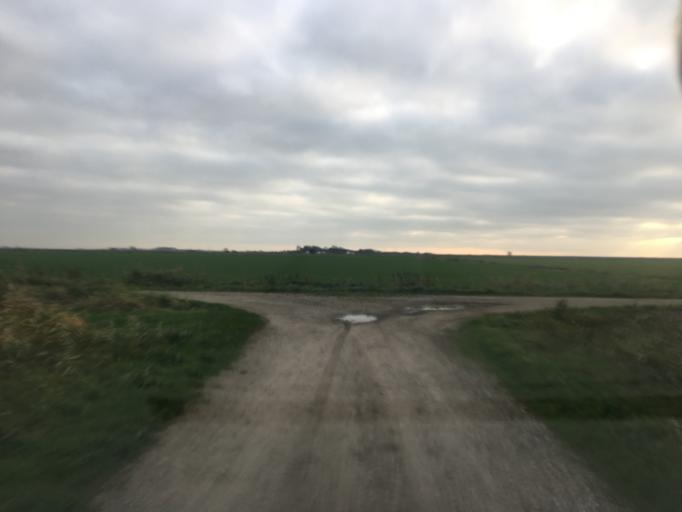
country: DE
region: Schleswig-Holstein
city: Rodenas
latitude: 54.9528
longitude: 8.7361
